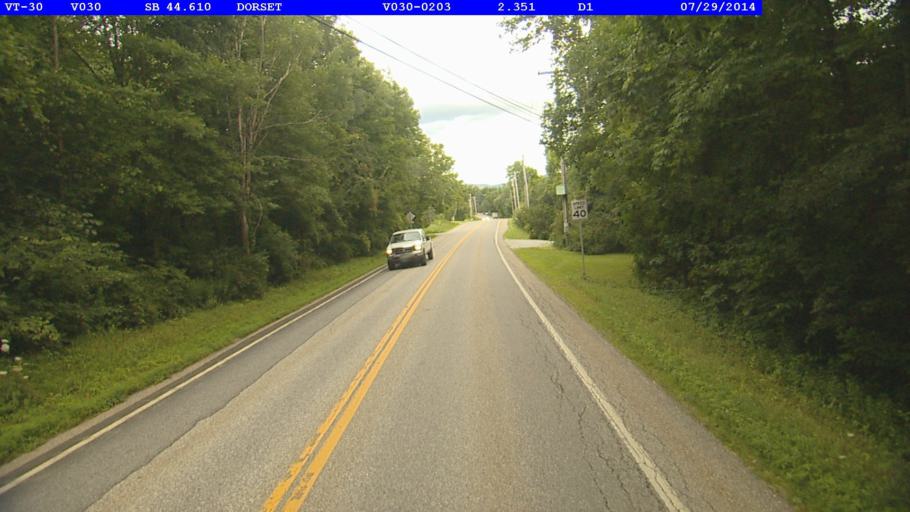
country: US
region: Vermont
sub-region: Bennington County
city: Manchester Center
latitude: 43.2422
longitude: -73.0889
